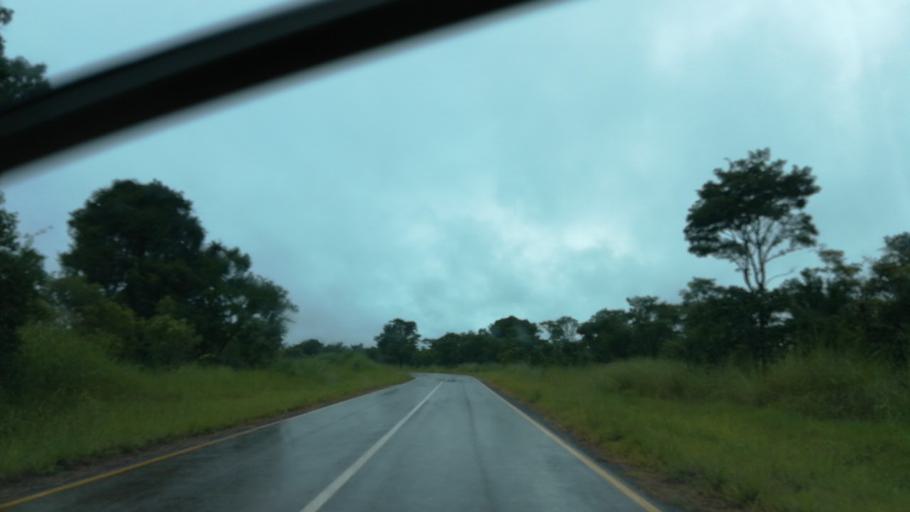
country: ZM
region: Luapula
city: Mwense
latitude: -10.8378
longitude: 28.2317
